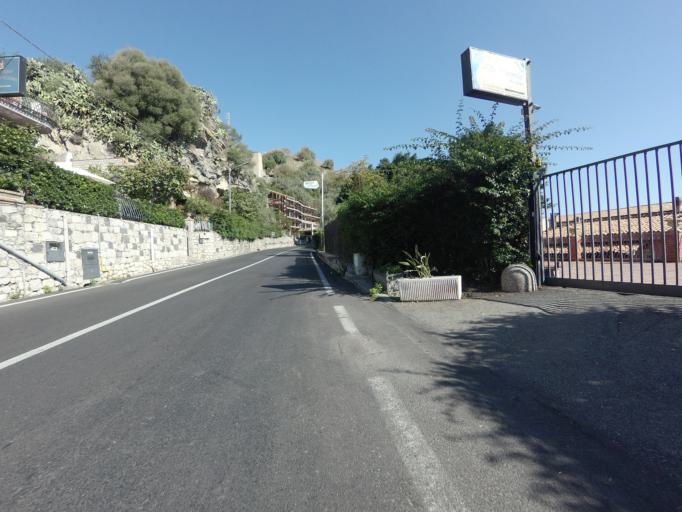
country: IT
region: Sicily
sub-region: Messina
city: Taormina
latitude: 37.8608
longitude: 15.2955
